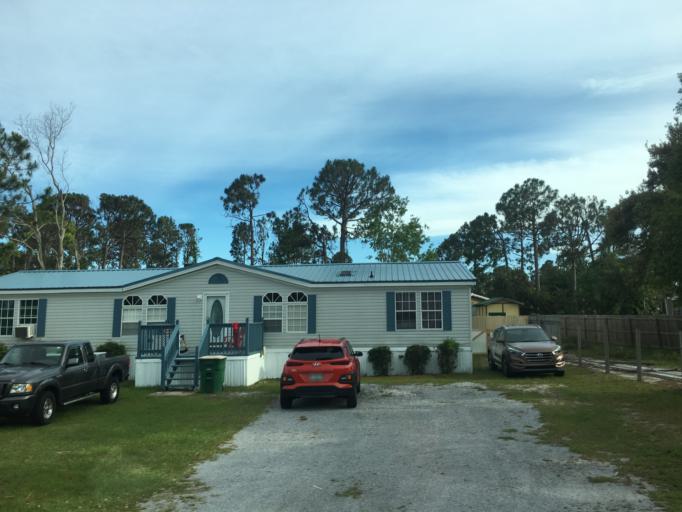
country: US
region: Florida
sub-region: Bay County
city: Upper Grand Lagoon
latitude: 30.1673
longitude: -85.7613
